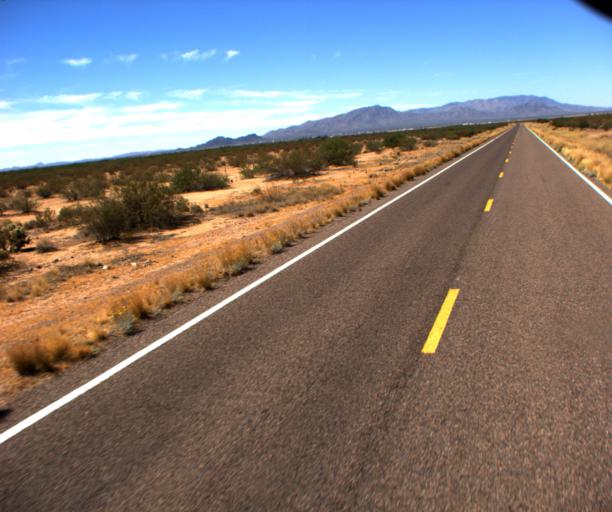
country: US
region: Arizona
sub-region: Yavapai County
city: Congress
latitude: 33.9975
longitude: -113.1249
